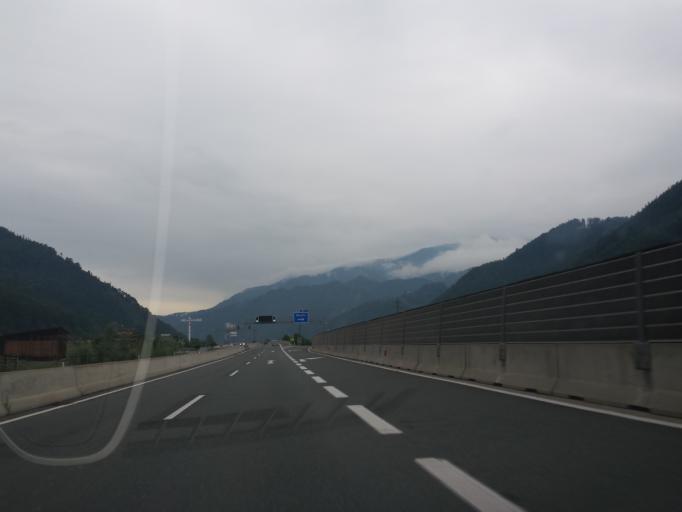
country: AT
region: Styria
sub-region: Politischer Bezirk Bruck-Muerzzuschlag
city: Pernegg an der Mur
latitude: 47.3400
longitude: 15.3505
